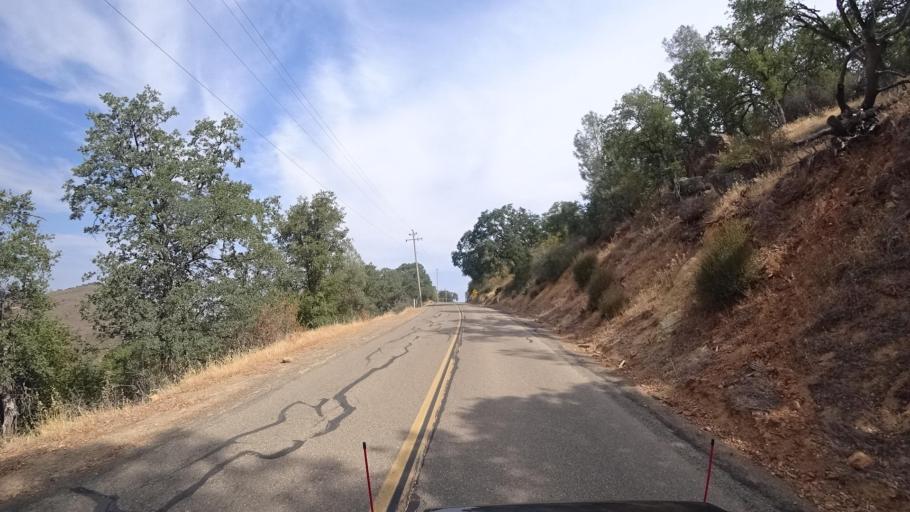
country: US
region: California
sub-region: Mariposa County
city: Mariposa
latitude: 37.5577
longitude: -120.0053
